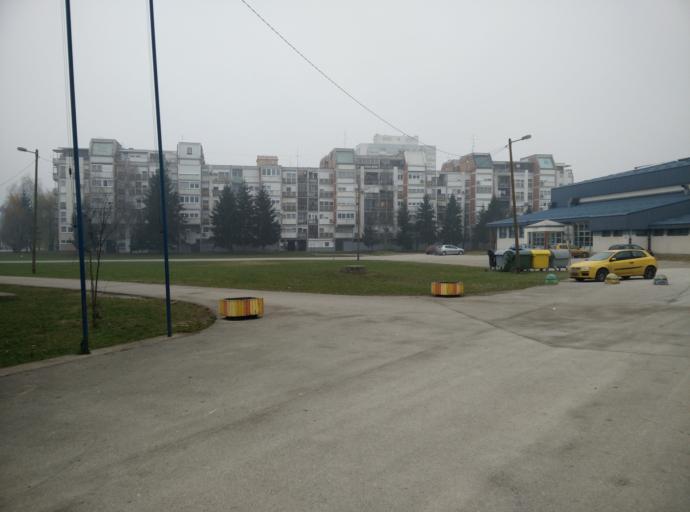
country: HR
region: Karlovacka
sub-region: Grad Karlovac
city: Karlovac
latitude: 45.4845
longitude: 15.5506
